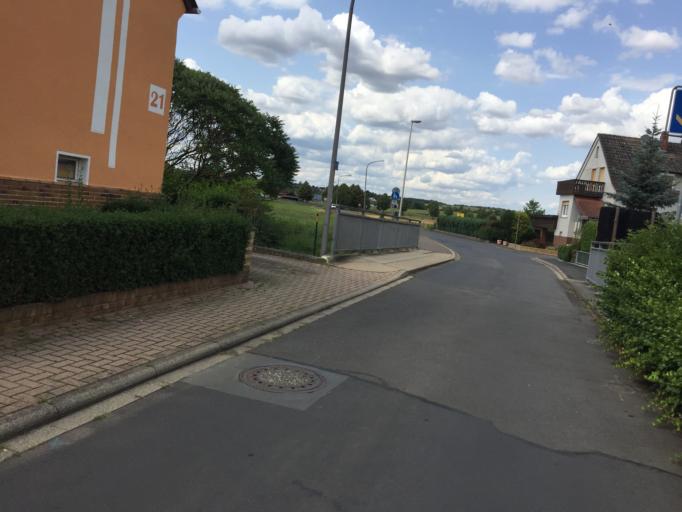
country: DE
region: Hesse
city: Schwalmstadt
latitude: 50.9145
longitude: 9.2527
